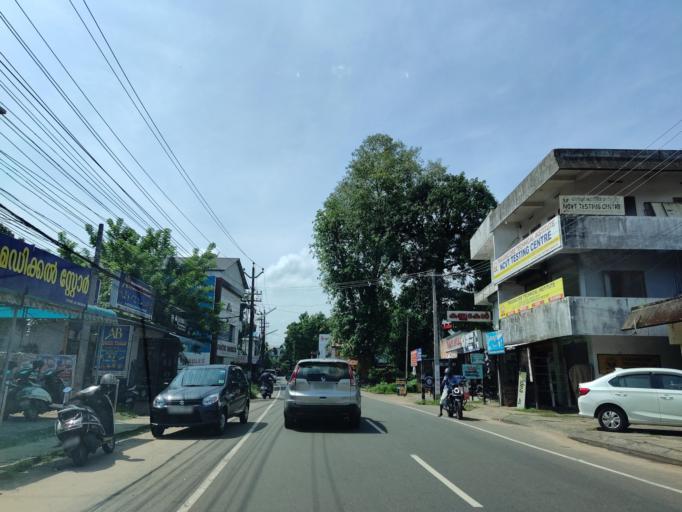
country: IN
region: Kerala
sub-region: Alappuzha
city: Mavelikara
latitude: 9.3120
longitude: 76.5341
